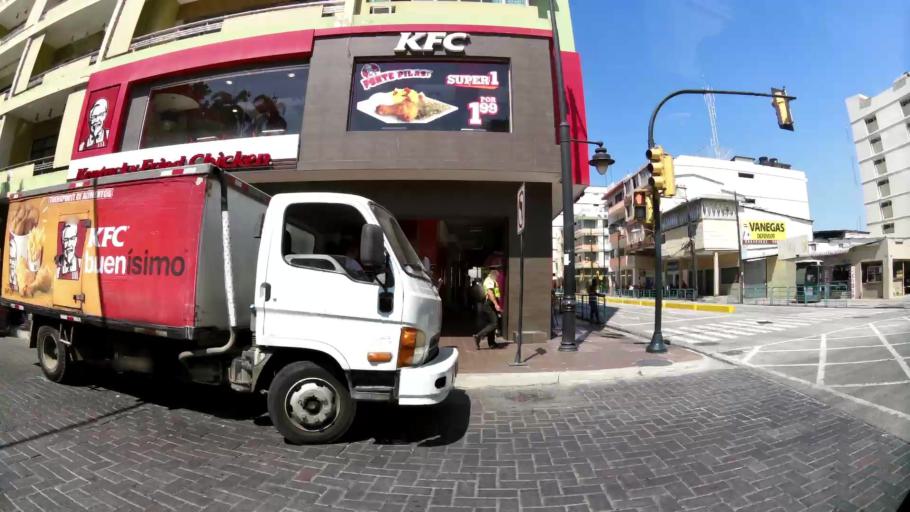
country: EC
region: Guayas
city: Guayaquil
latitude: -2.1908
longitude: -79.8887
